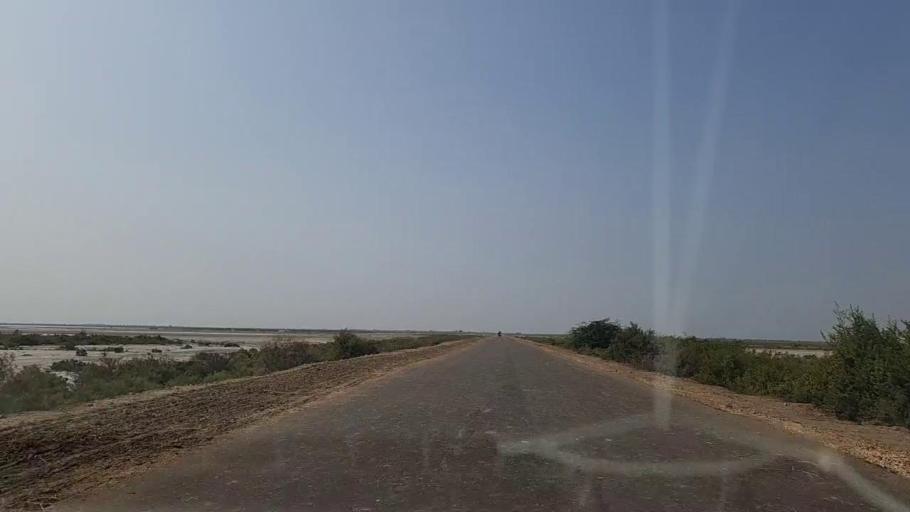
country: PK
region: Sindh
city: Chuhar Jamali
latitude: 24.2222
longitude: 67.8944
